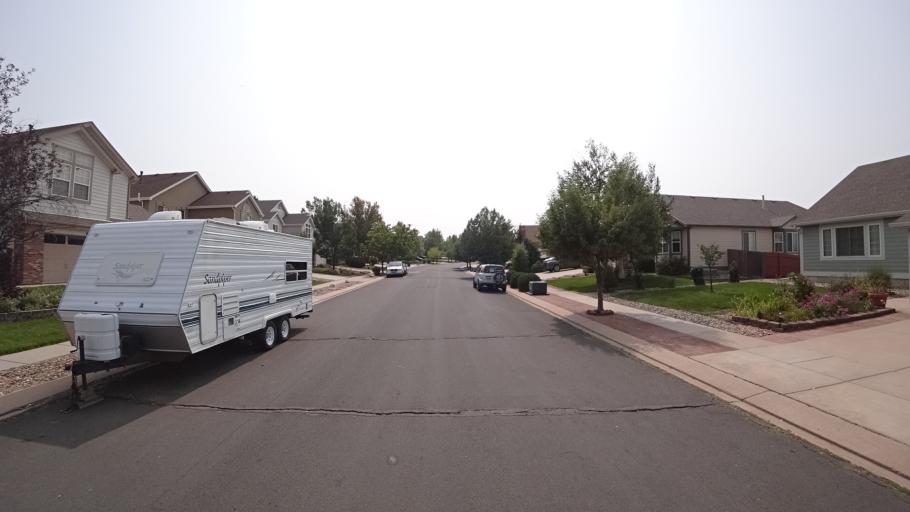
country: US
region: Colorado
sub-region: El Paso County
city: Cimarron Hills
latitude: 38.9258
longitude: -104.7478
